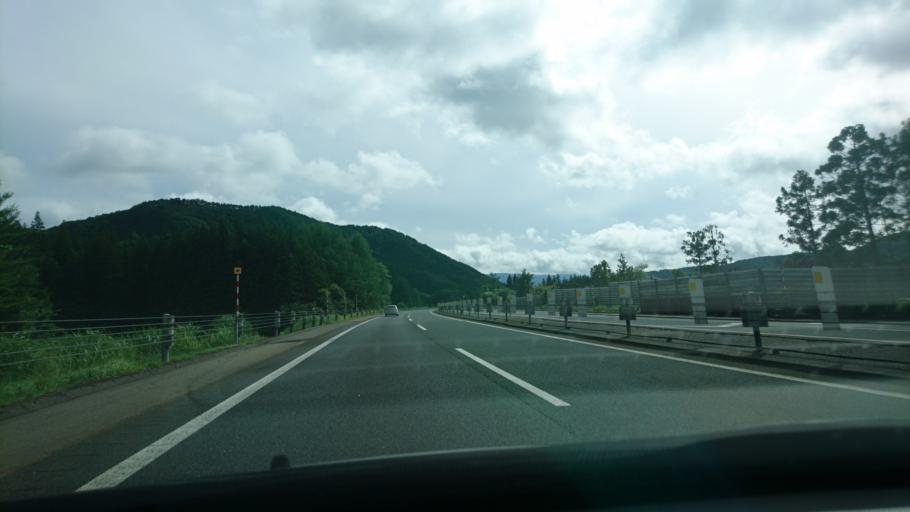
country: JP
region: Akita
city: Hanawa
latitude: 40.0534
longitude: 141.0157
